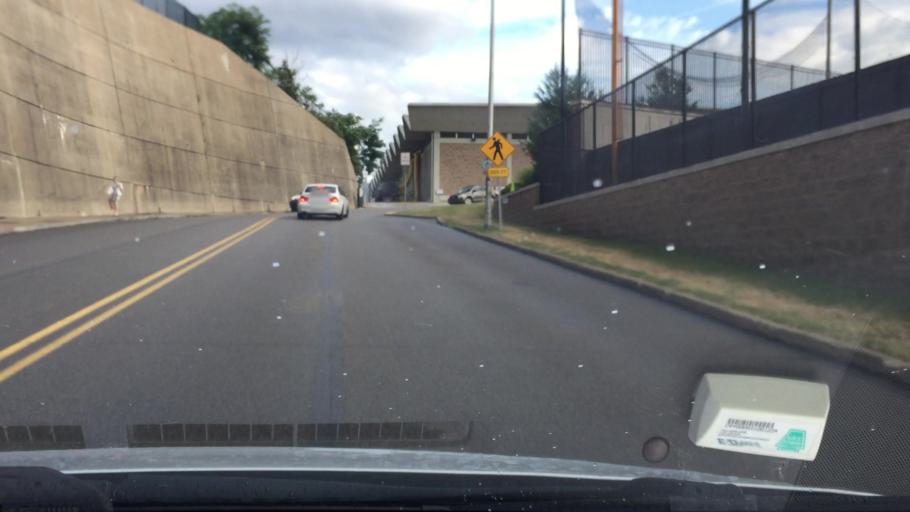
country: US
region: Pennsylvania
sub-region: Allegheny County
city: Bloomfield
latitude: 40.4455
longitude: -79.9654
